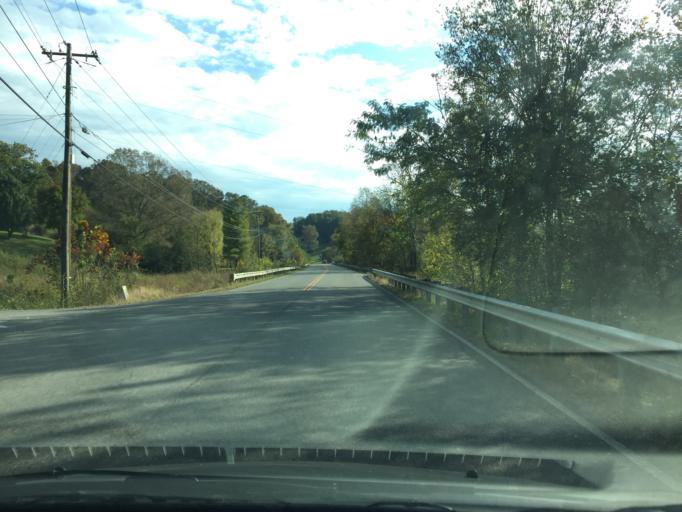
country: US
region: Tennessee
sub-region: Loudon County
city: Loudon
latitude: 35.7054
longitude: -84.3437
